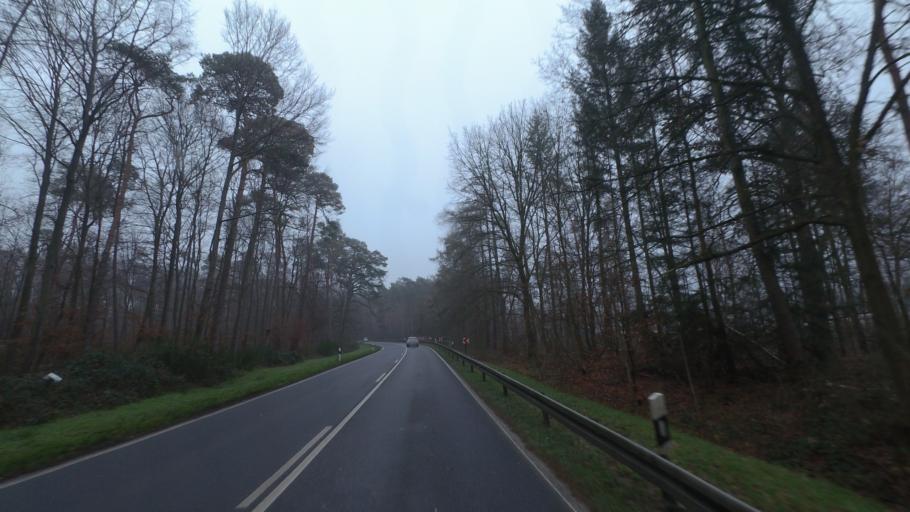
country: DE
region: Hesse
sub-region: Regierungsbezirk Darmstadt
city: Rodgau
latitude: 50.0573
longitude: 8.9075
